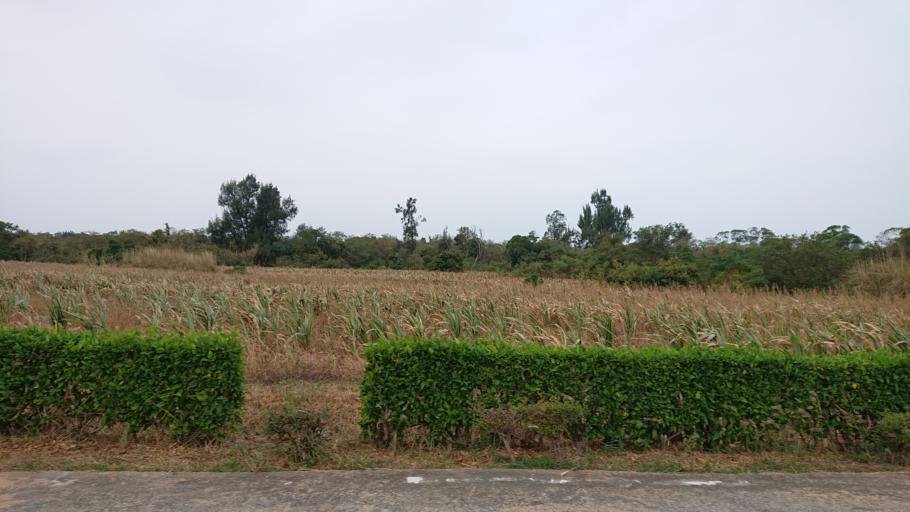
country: TW
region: Fukien
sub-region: Kinmen
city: Jincheng
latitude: 24.4543
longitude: 118.3597
